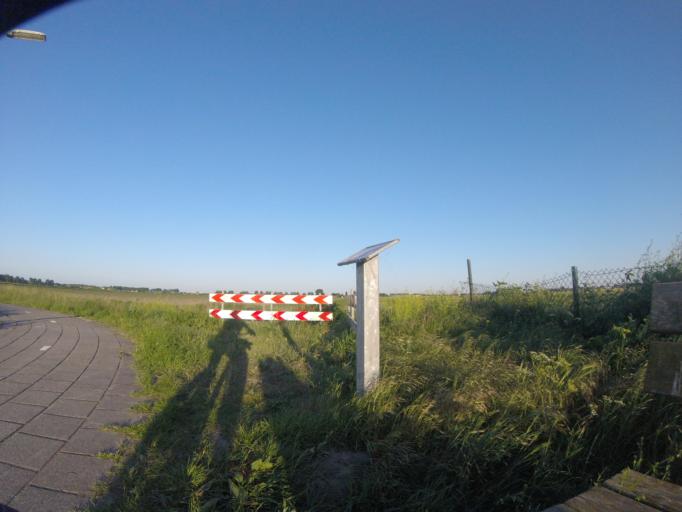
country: NL
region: North Holland
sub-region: Gemeente Haarlemmermeer
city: Hoofddorp
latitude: 52.3714
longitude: 4.7273
